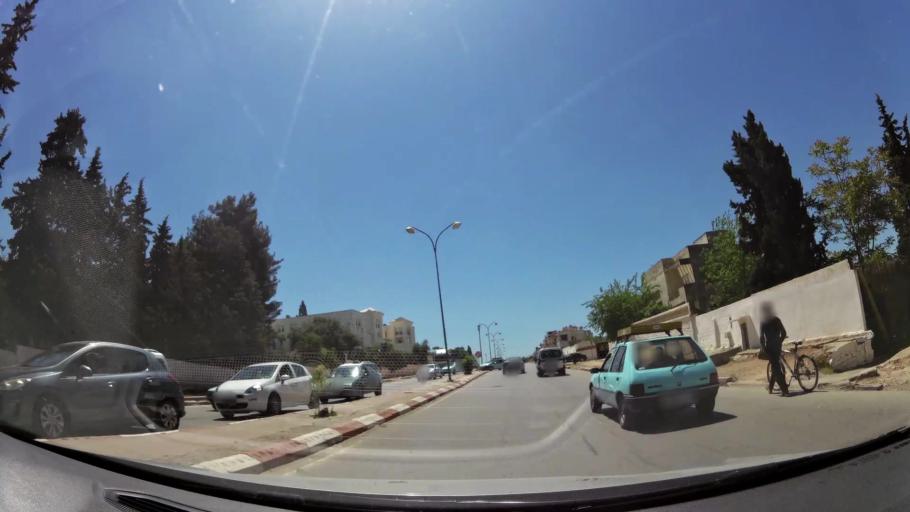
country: MA
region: Meknes-Tafilalet
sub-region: Meknes
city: Meknes
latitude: 33.8937
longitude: -5.5487
